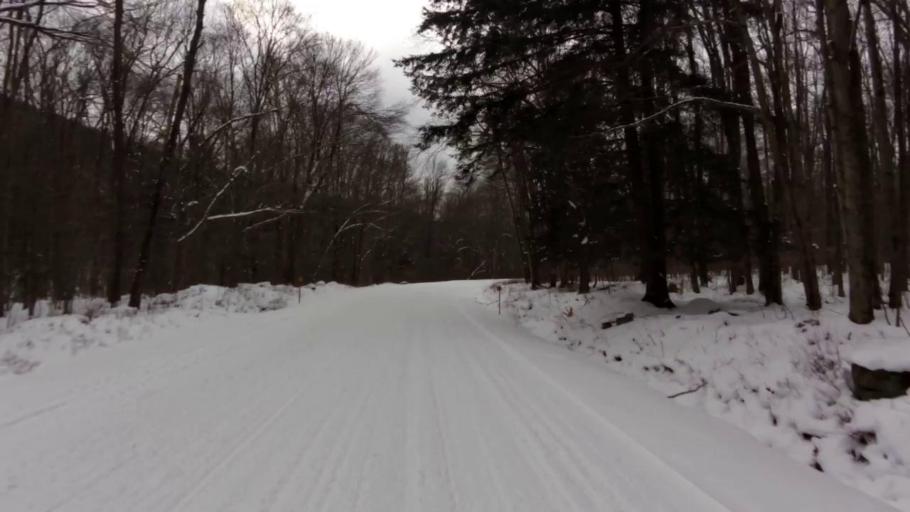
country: US
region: New York
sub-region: Cattaraugus County
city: Salamanca
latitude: 42.0229
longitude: -78.8159
